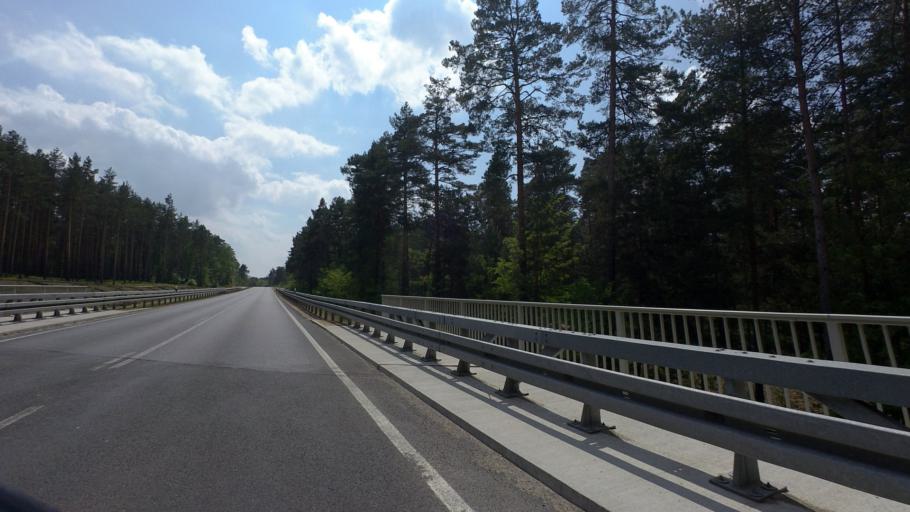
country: DE
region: Saxony
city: Rietschen
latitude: 51.4199
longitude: 14.7891
